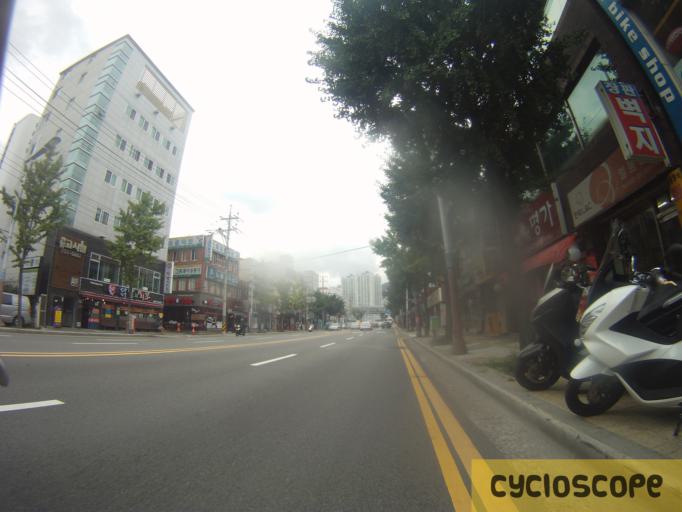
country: KR
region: Busan
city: Busan
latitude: 35.1716
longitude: 129.1087
